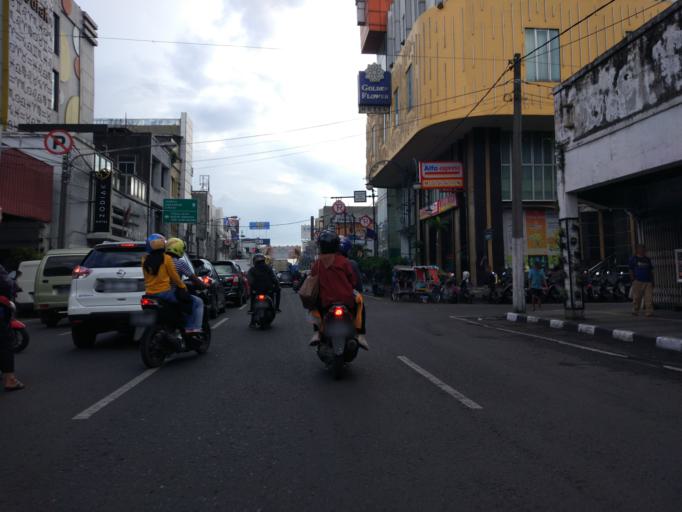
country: ID
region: West Java
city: Bandung
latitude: -6.9209
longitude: 107.6054
